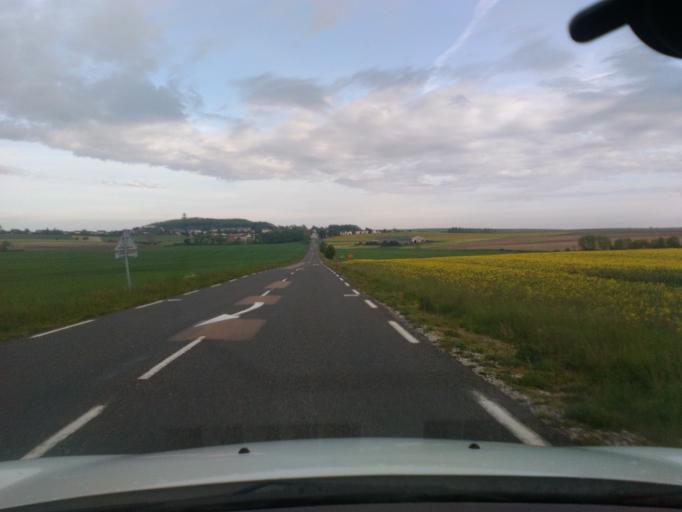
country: FR
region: Champagne-Ardenne
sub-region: Departement de la Haute-Marne
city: Lavilleneuve-au-Roi
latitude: 48.2166
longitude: 4.9070
